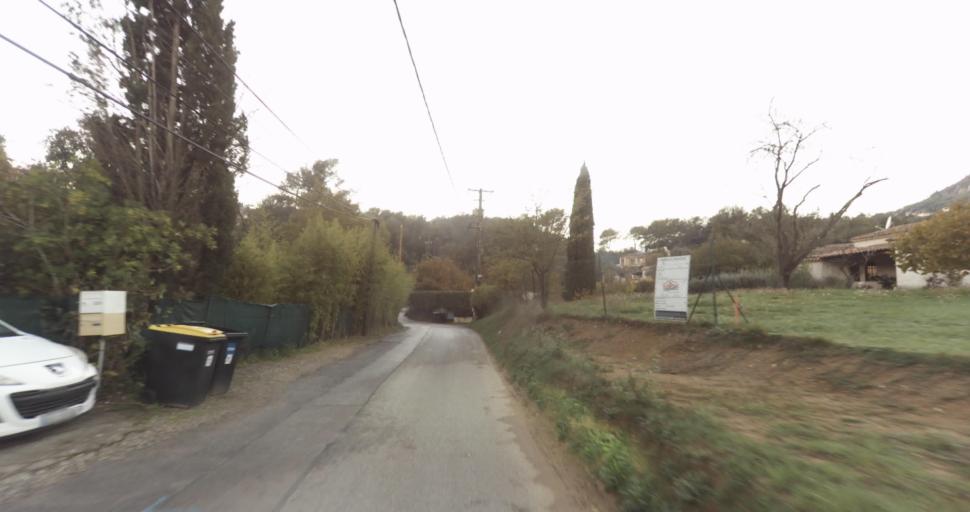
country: FR
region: Provence-Alpes-Cote d'Azur
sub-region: Departement des Alpes-Maritimes
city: Vence
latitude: 43.7248
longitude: 7.1272
